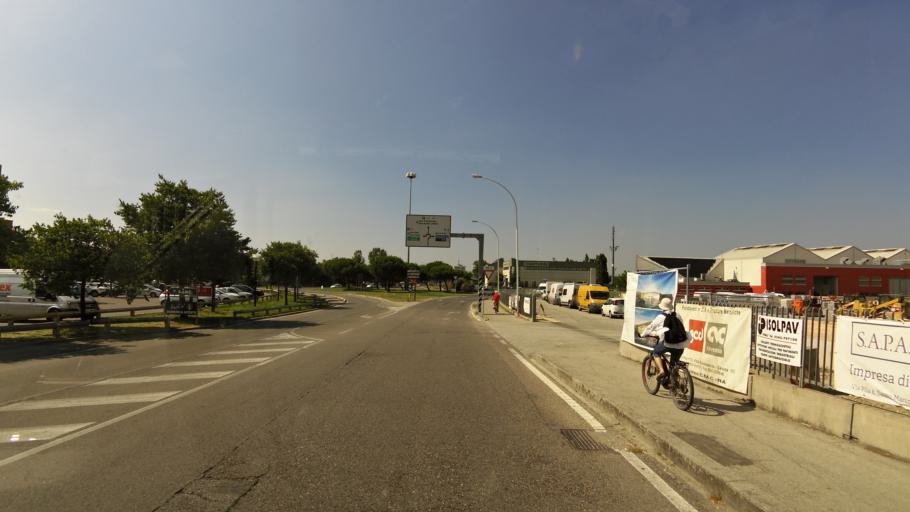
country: IT
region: Emilia-Romagna
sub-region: Provincia di Ravenna
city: Ravenna
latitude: 44.3998
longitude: 12.2147
